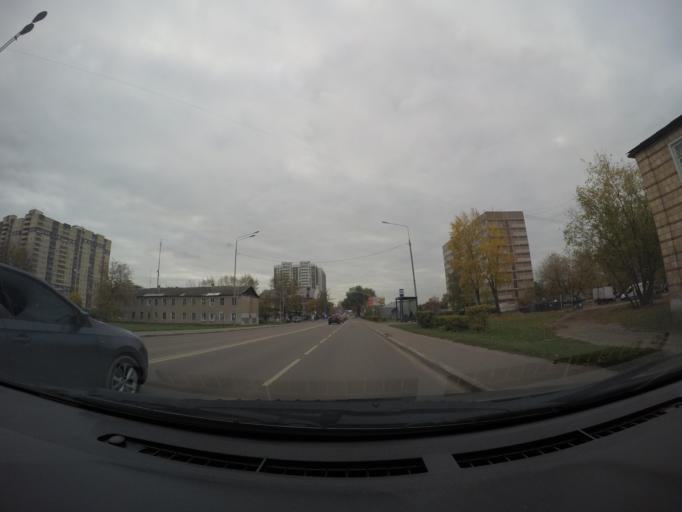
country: RU
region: Moskovskaya
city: Staraya Kupavna
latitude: 55.8044
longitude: 38.1804
